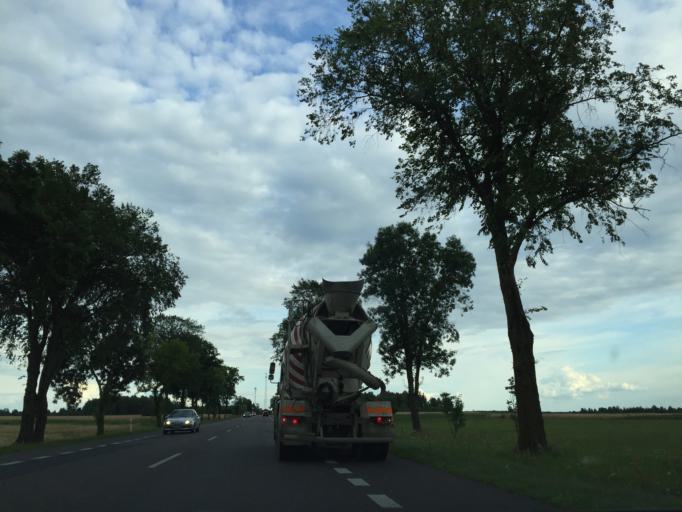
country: PL
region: Lublin Voivodeship
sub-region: Powiat lubartowski
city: Firlej
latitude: 51.5716
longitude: 22.4981
